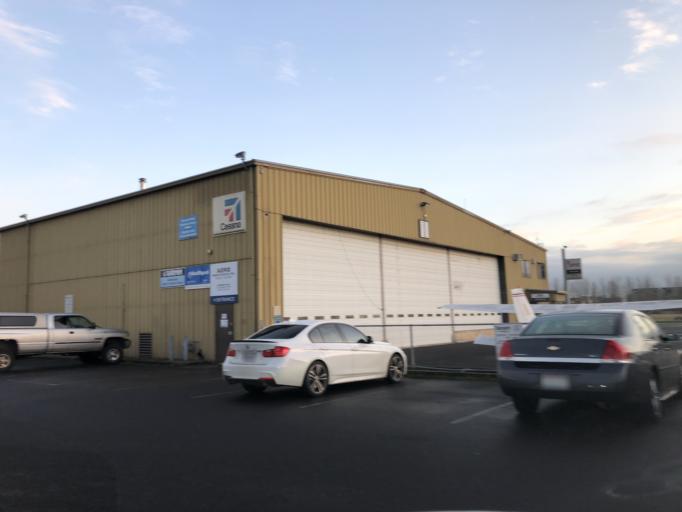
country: US
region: Washington
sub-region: Clark County
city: Vancouver
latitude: 45.6223
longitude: -122.6559
